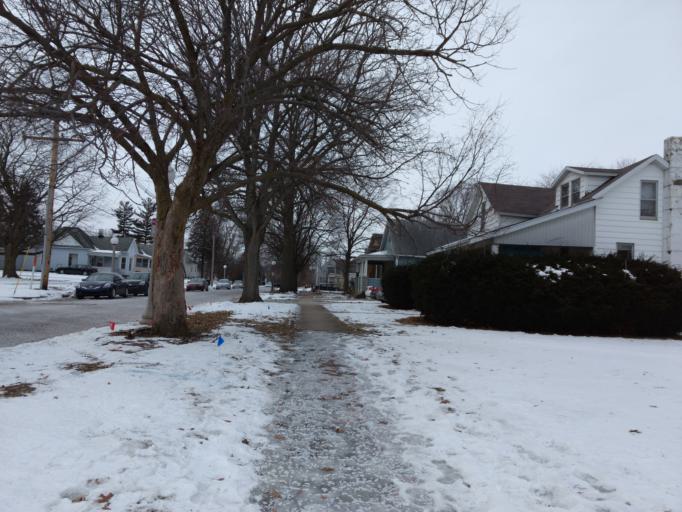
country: US
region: Illinois
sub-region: Champaign County
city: Urbana
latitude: 40.1155
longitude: -88.2176
